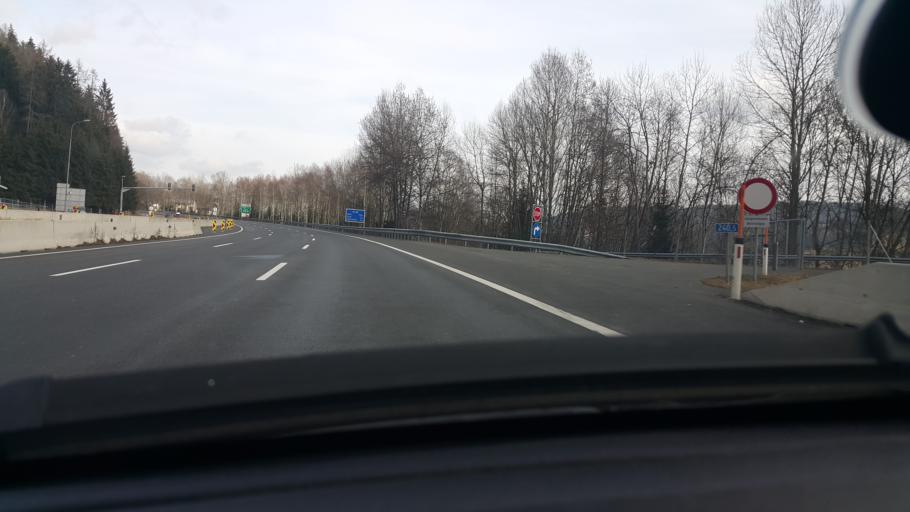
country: AT
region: Carinthia
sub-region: Politischer Bezirk Wolfsberg
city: Preitenegg
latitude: 46.9343
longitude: 14.8613
